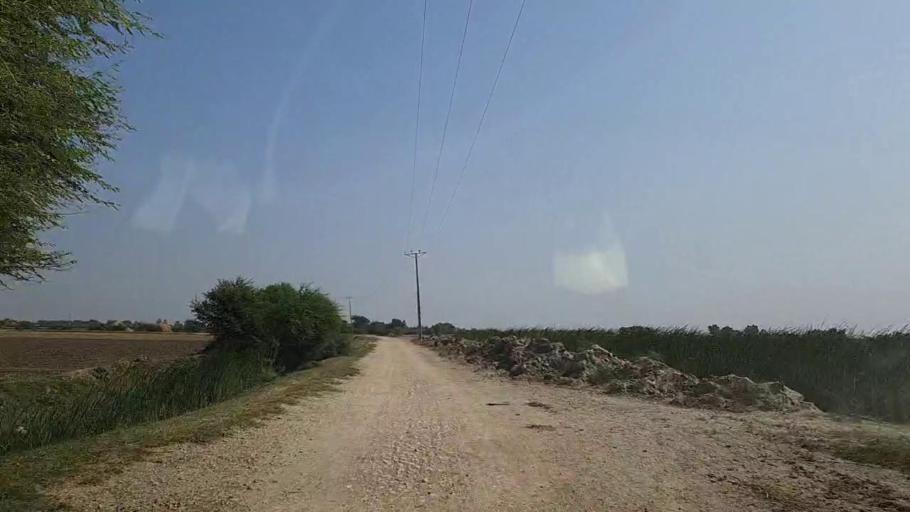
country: PK
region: Sindh
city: Mirpur Sakro
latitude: 24.5264
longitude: 67.8061
